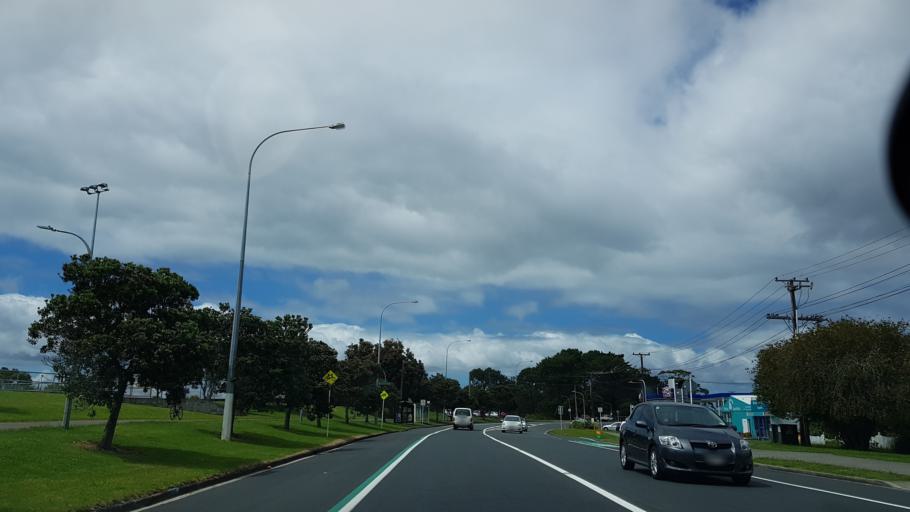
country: NZ
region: Auckland
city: Murrays Bay
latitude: -36.7569
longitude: 174.7511
